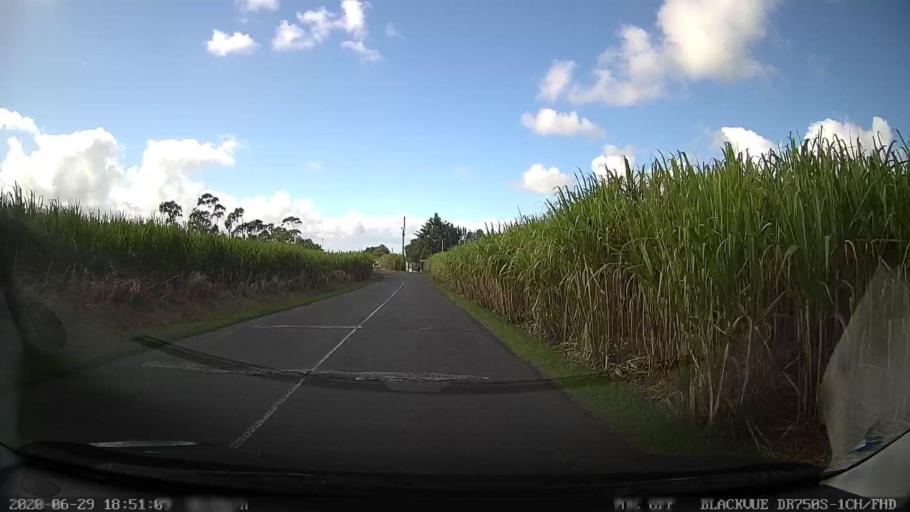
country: RE
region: Reunion
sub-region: Reunion
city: Bras-Panon
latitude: -20.9895
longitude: 55.6599
